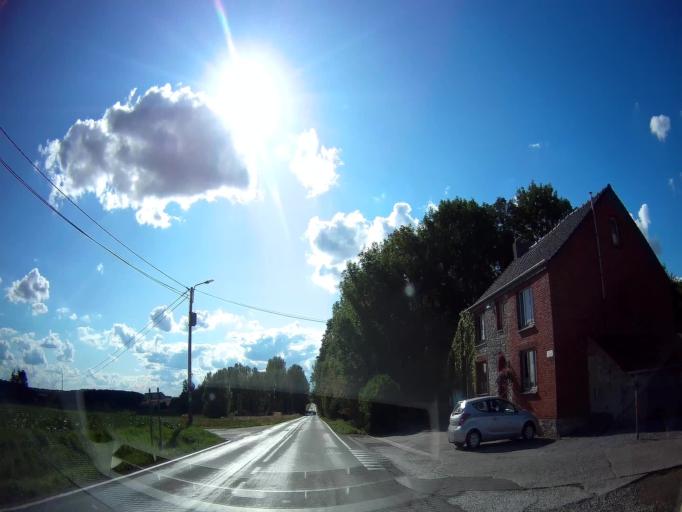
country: BE
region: Wallonia
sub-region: Province de Namur
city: Mettet
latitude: 50.3163
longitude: 4.7135
